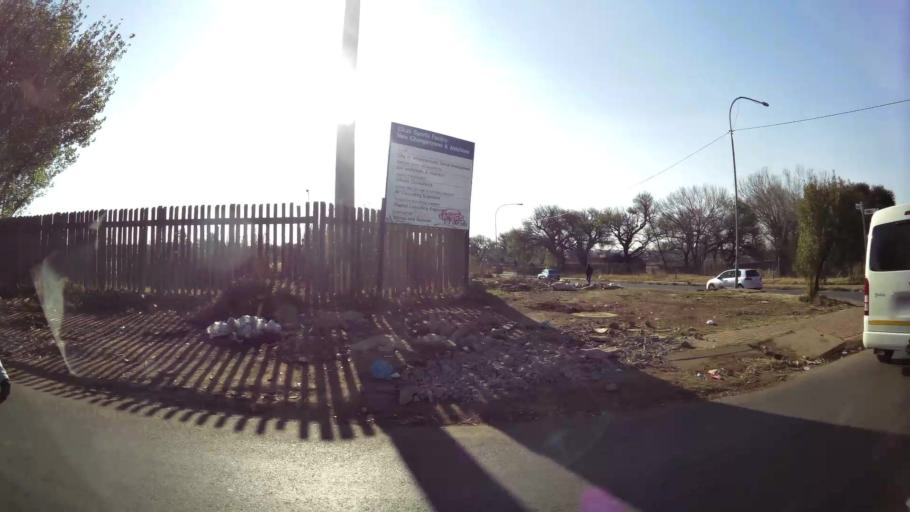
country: ZA
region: Gauteng
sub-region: City of Johannesburg Metropolitan Municipality
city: Soweto
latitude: -26.2642
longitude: 27.8702
